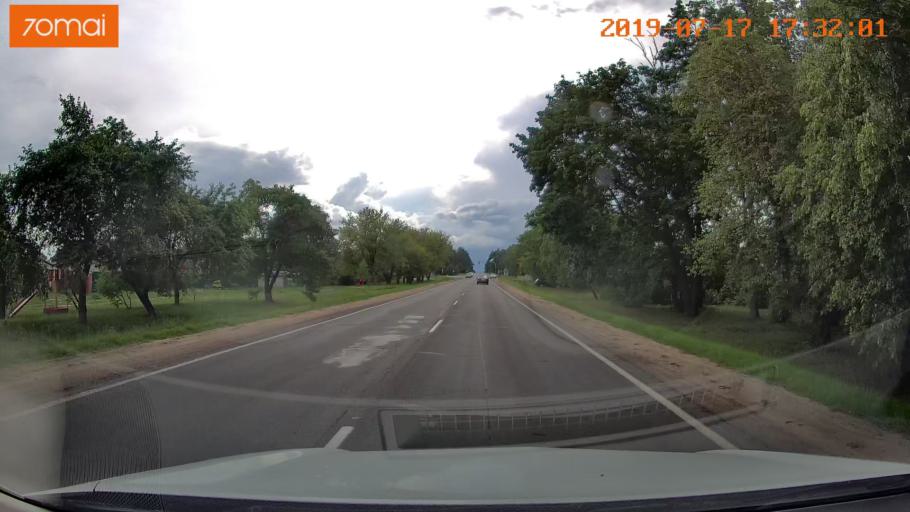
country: BY
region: Mogilev
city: Babruysk
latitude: 53.1148
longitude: 29.1140
